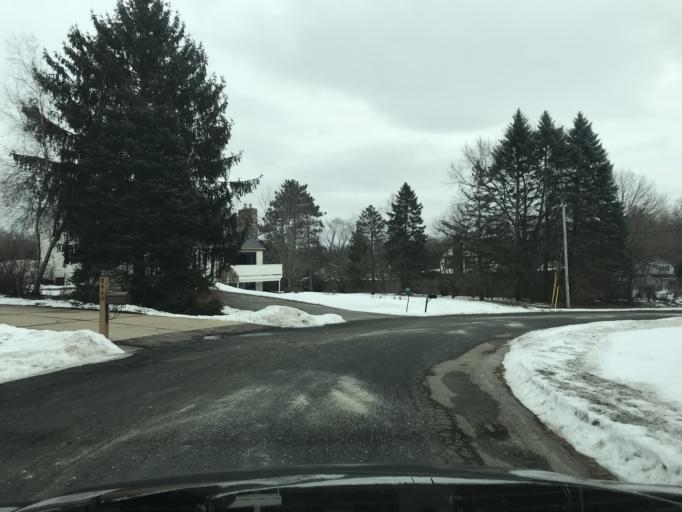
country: US
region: Wisconsin
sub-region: Dane County
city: Monona
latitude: 43.0831
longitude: -89.2686
